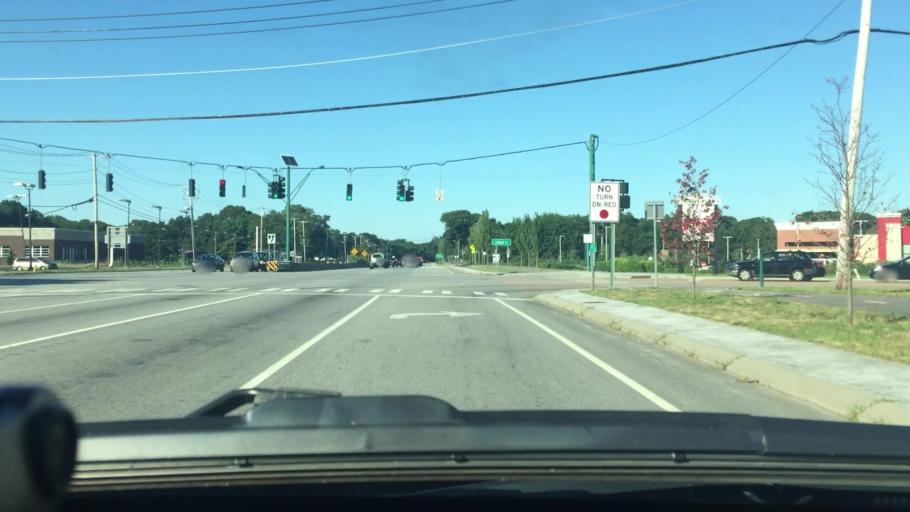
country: US
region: New York
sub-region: Suffolk County
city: Port Jefferson Station
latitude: 40.9258
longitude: -73.0455
